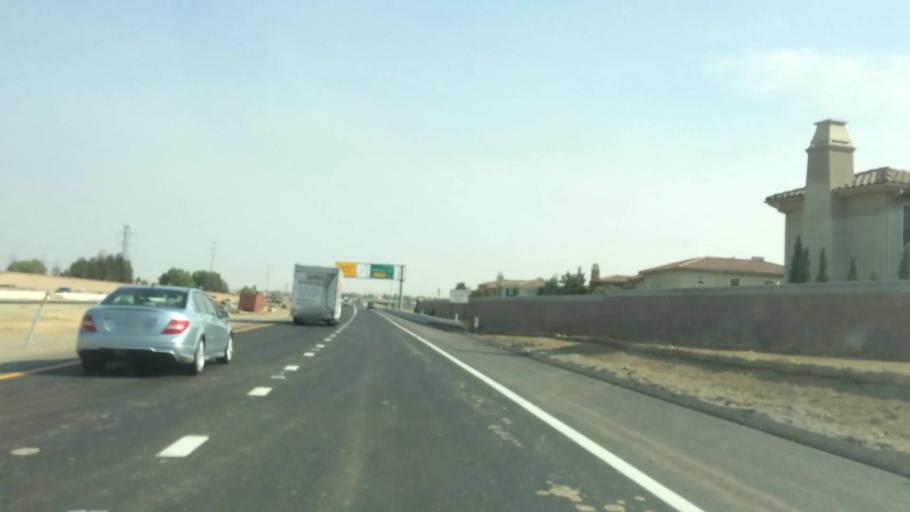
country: US
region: California
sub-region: Contra Costa County
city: Brentwood
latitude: 37.9350
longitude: -121.7378
